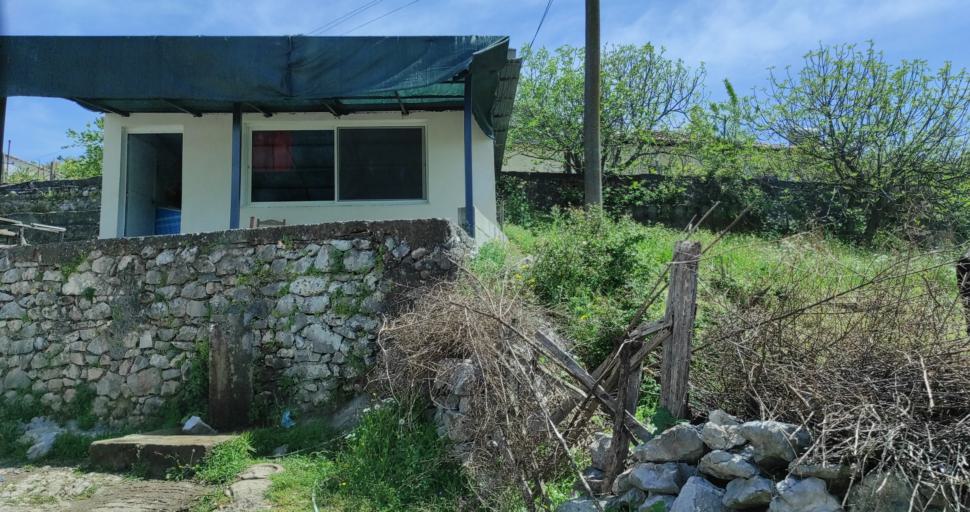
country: AL
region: Shkoder
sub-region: Rrethi i Malesia e Madhe
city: Gruemire
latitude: 42.1416
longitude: 19.5475
